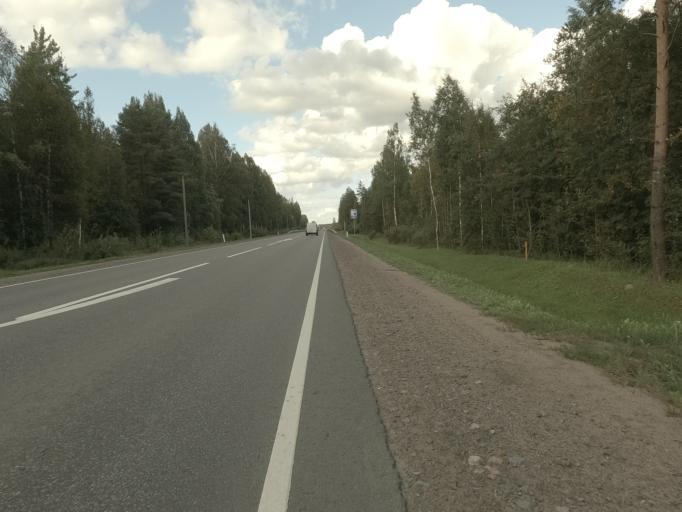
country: RU
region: Leningrad
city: Mga
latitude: 59.7397
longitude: 31.0763
